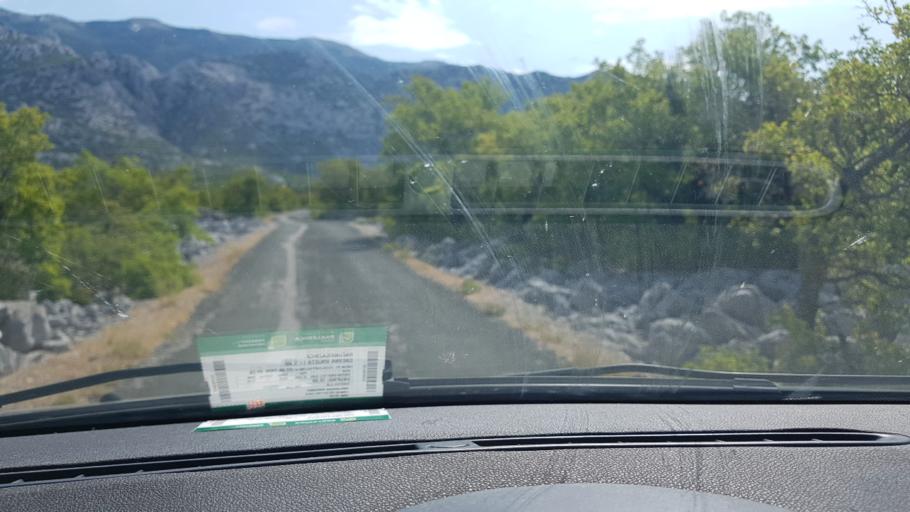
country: HR
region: Licko-Senjska
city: Novalja
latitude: 44.6938
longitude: 14.9209
